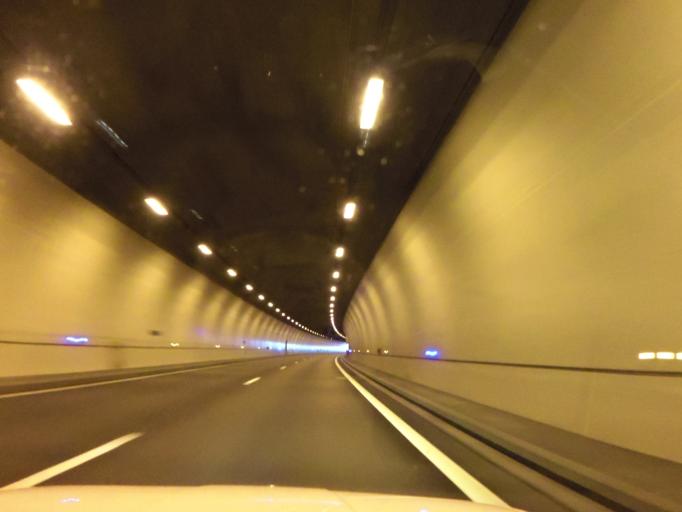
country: FR
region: Rhone-Alpes
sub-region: Departement de la Savoie
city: Aiton
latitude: 45.5366
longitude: 6.3068
